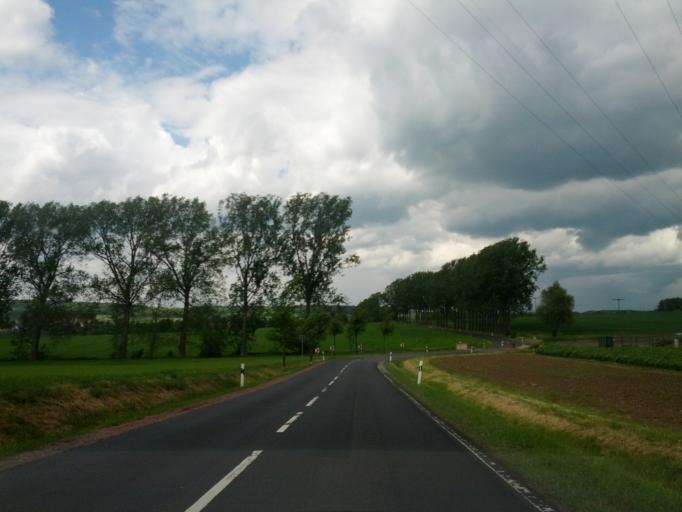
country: DE
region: Thuringia
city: Friedrichswerth
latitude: 51.0155
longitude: 10.5331
